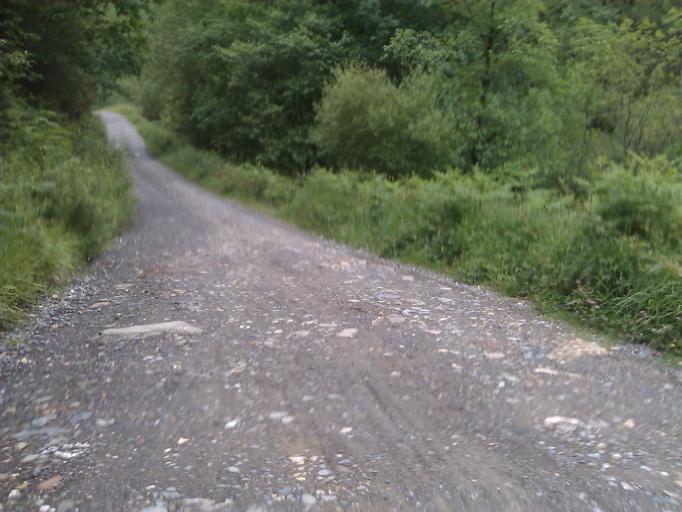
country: ES
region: Basque Country
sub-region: Provincia de Guipuzcoa
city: Elduayen
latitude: 43.1739
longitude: -1.9850
